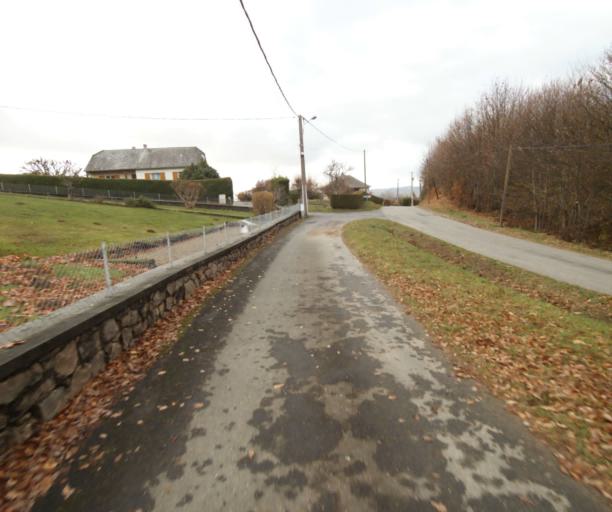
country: FR
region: Limousin
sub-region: Departement de la Correze
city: Sainte-Fortunade
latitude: 45.2061
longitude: 1.7805
